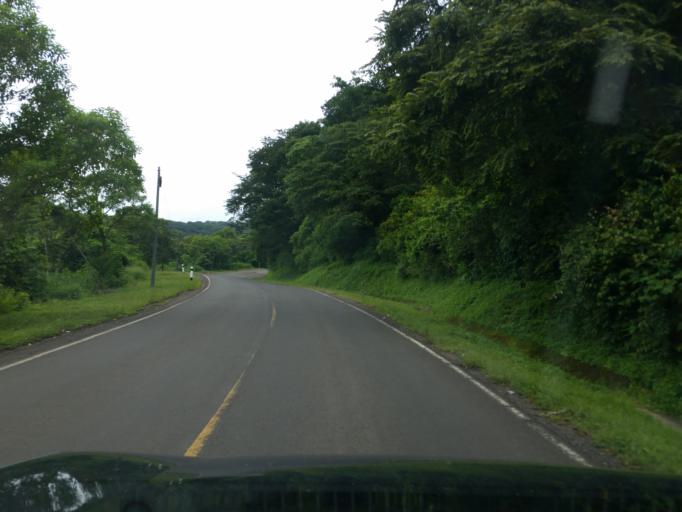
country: NI
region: Matagalpa
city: San Ramon
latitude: 12.9737
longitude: -85.8501
